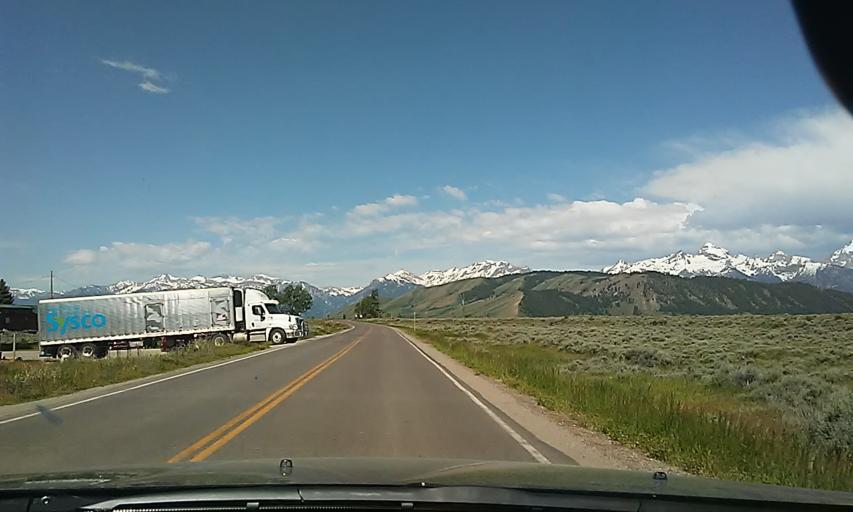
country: US
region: Wyoming
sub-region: Teton County
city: Jackson
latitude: 43.6252
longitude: -110.6270
